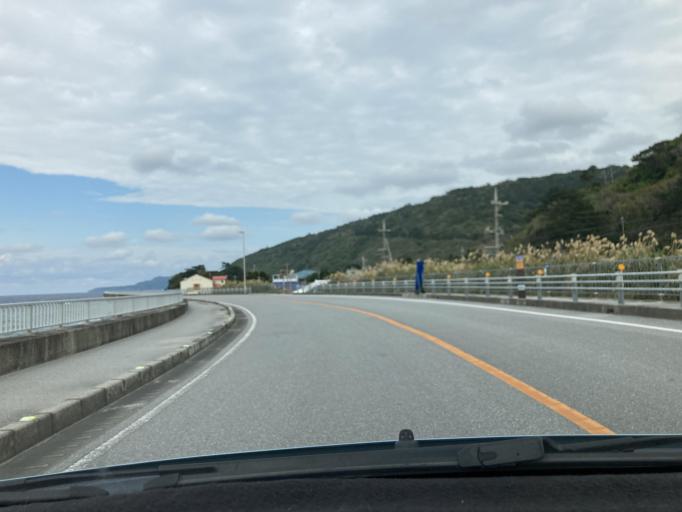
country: JP
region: Okinawa
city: Nago
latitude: 26.7841
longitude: 128.2187
